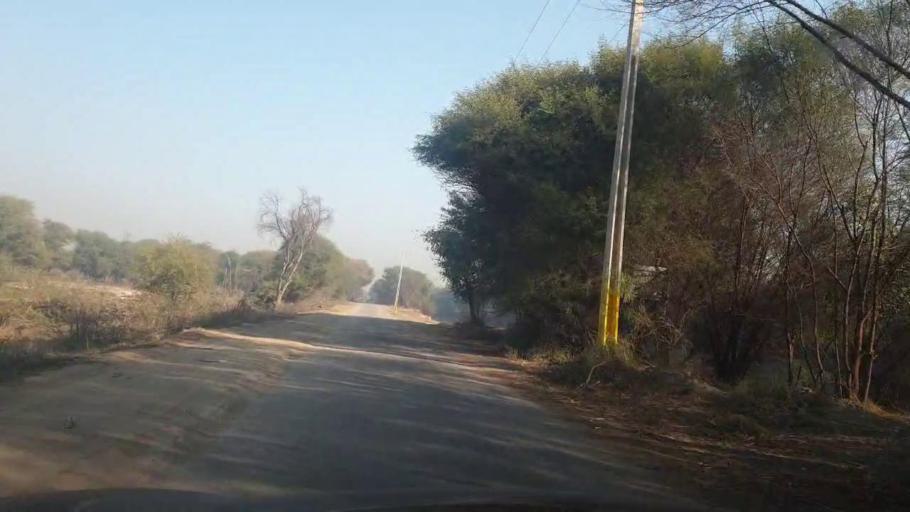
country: PK
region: Sindh
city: Mirpur Mathelo
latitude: 28.0543
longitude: 69.4619
